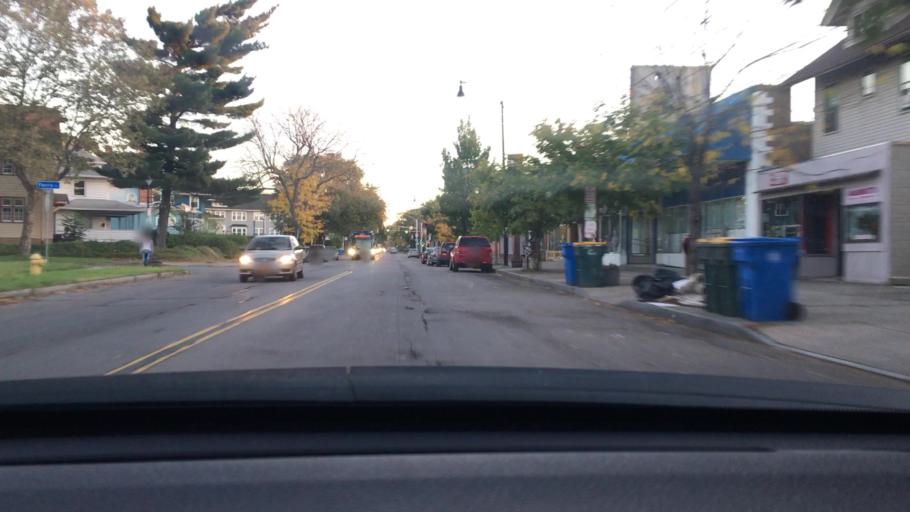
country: US
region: New York
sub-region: Monroe County
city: Brighton
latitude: 43.1696
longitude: -77.5609
